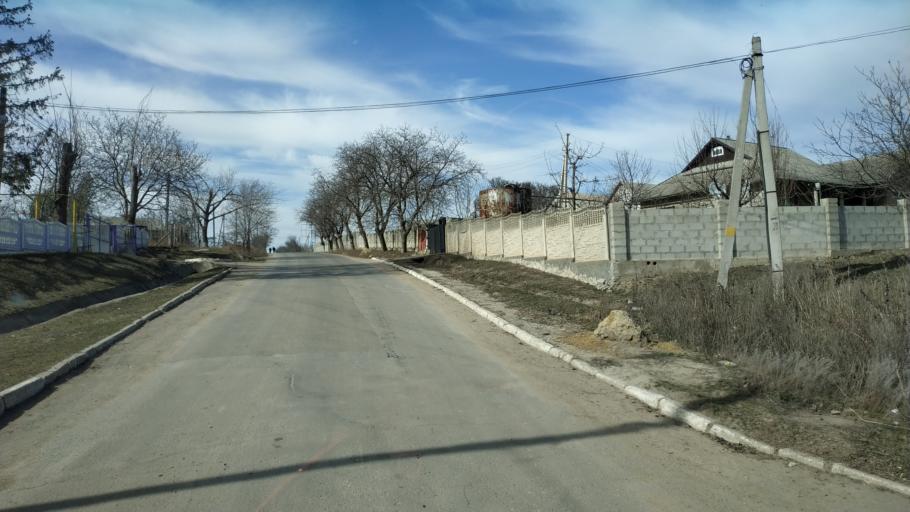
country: MD
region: Nisporeni
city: Nisporeni
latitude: 46.9631
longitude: 28.2106
